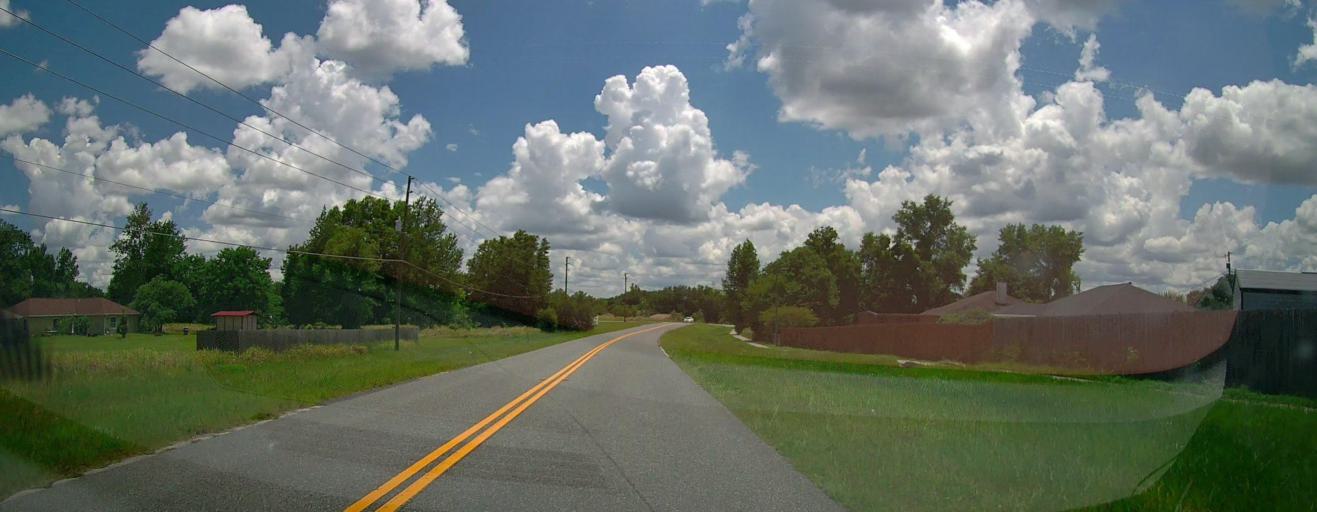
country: US
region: Florida
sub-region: Marion County
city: Silver Springs Shores
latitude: 29.1414
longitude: -82.0389
